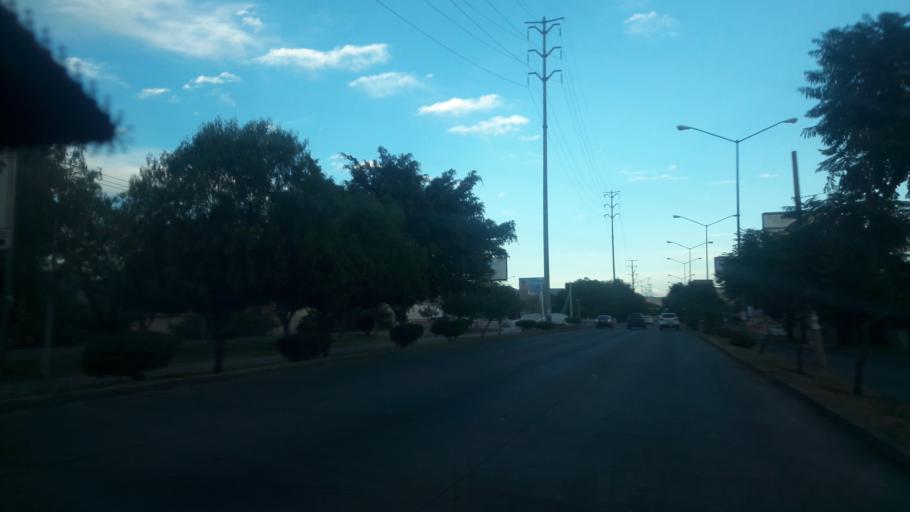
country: MX
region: Guanajuato
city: Leon
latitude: 21.1534
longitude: -101.6792
